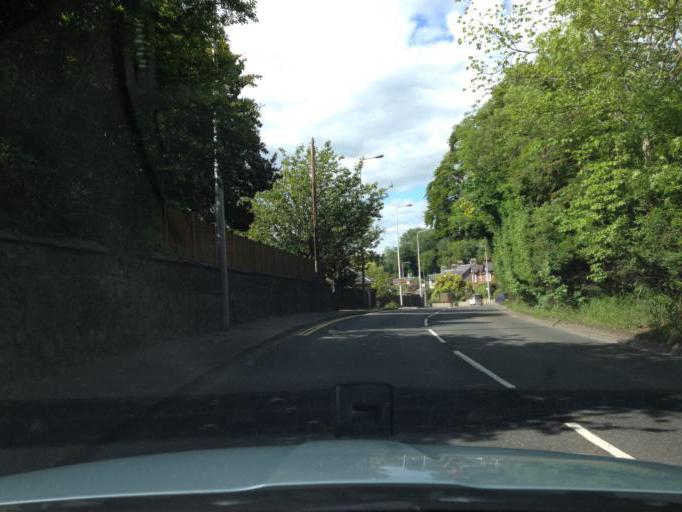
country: GB
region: Scotland
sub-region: Perth and Kinross
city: Perth
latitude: 56.3883
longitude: -3.4193
